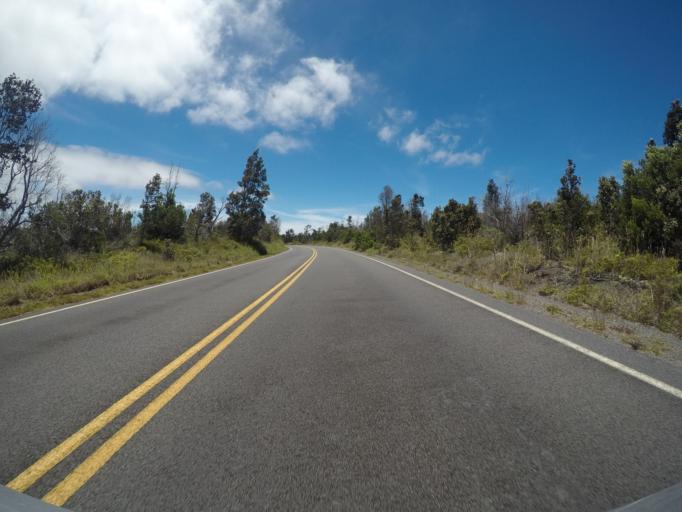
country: US
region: Hawaii
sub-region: Hawaii County
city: Volcano
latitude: 19.3727
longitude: -155.2341
